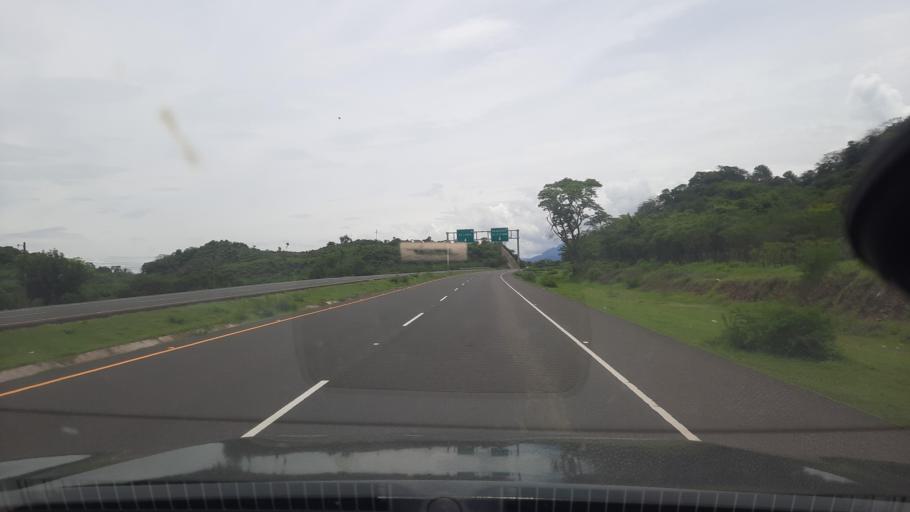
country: HN
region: Valle
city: Aramecina
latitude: 13.6783
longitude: -87.7305
